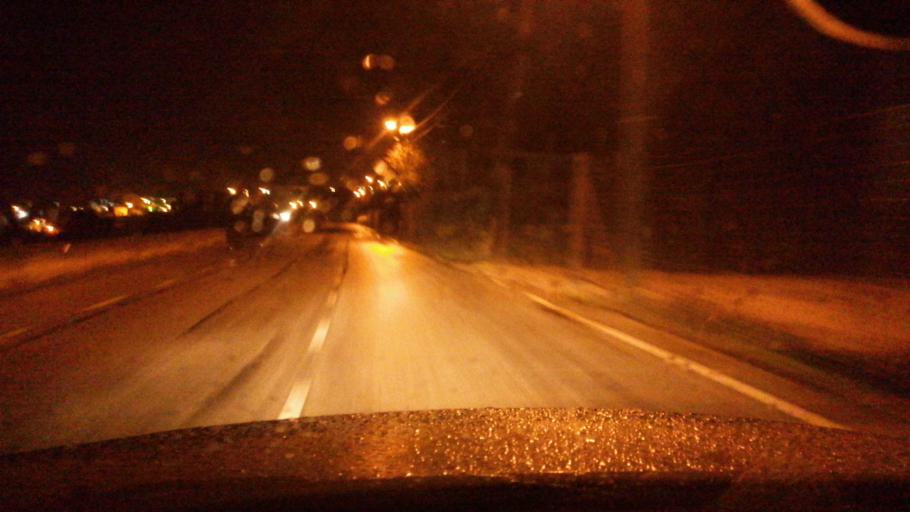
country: PT
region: Viseu
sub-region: Armamar
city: Armamar
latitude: 41.0994
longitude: -7.6857
